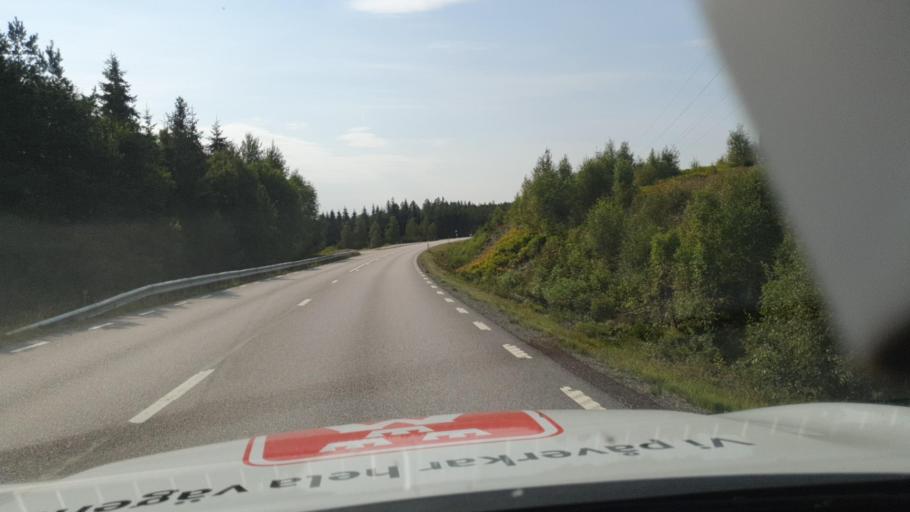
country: SE
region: Vaestra Goetaland
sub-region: Dals-Ed Kommun
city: Ed
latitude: 58.8557
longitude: 11.7771
